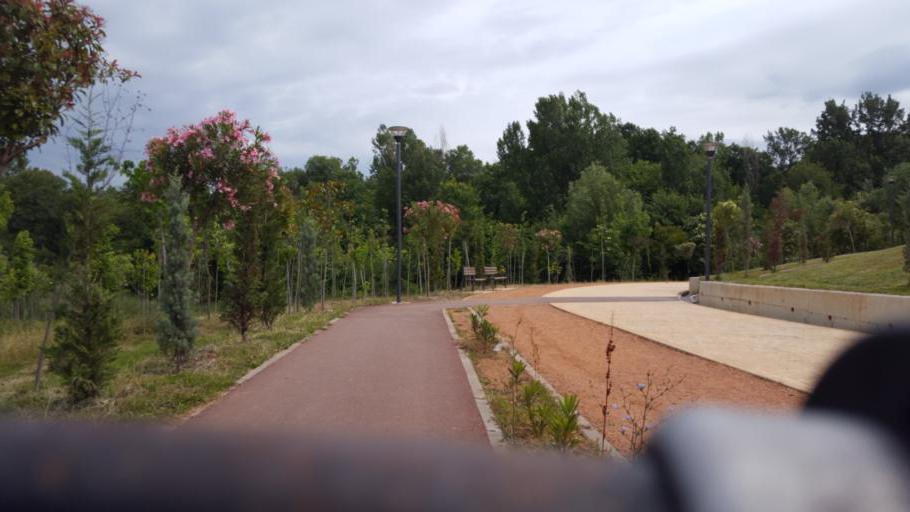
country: AL
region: Tirane
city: Tirana
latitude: 41.3060
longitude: 19.8246
